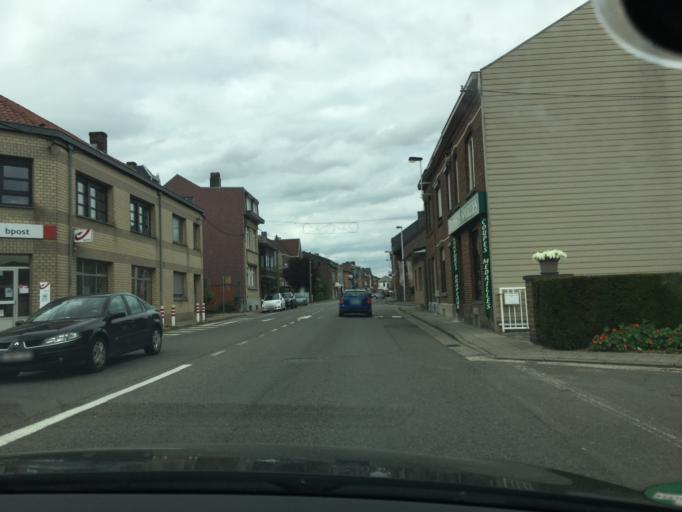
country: BE
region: Wallonia
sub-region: Province de Liege
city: Soumagne
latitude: 50.6298
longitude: 5.7307
